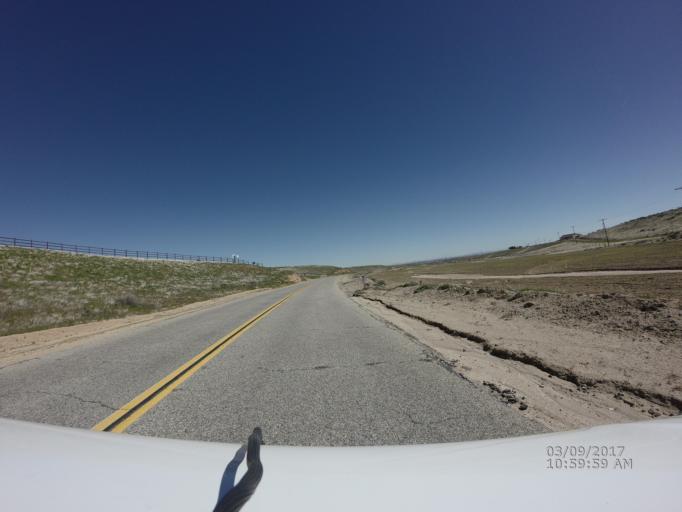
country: US
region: California
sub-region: Los Angeles County
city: Green Valley
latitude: 34.7035
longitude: -118.3739
